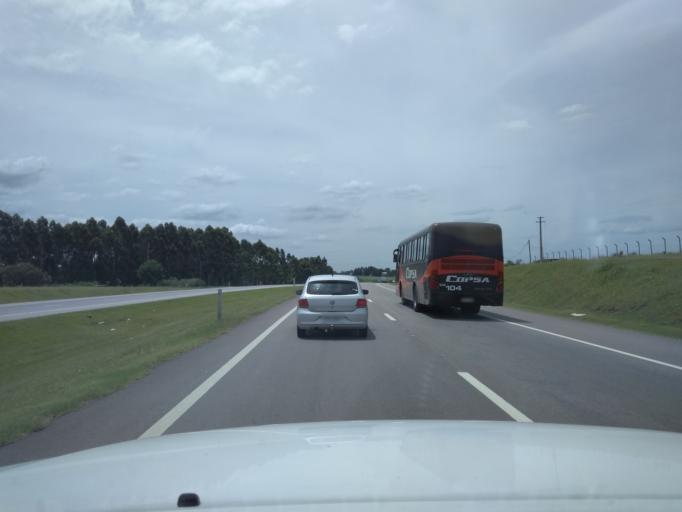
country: UY
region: Canelones
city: Progreso
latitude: -34.6850
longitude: -56.2404
